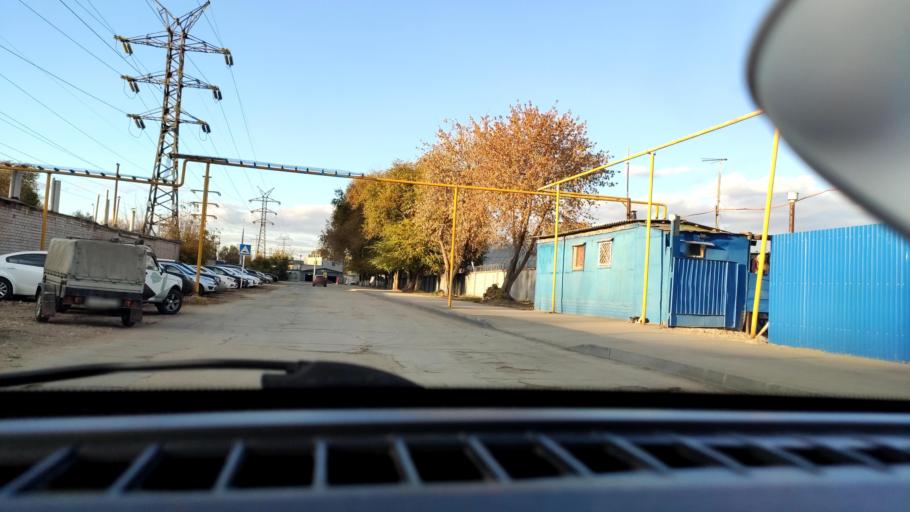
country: RU
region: Samara
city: Smyshlyayevka
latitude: 53.2097
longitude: 50.2864
